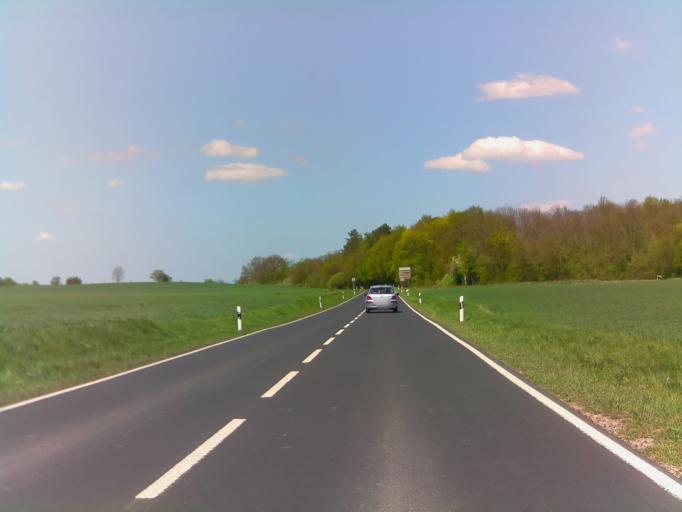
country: DE
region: Thuringia
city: Dornheim
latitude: 50.8096
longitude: 10.9766
